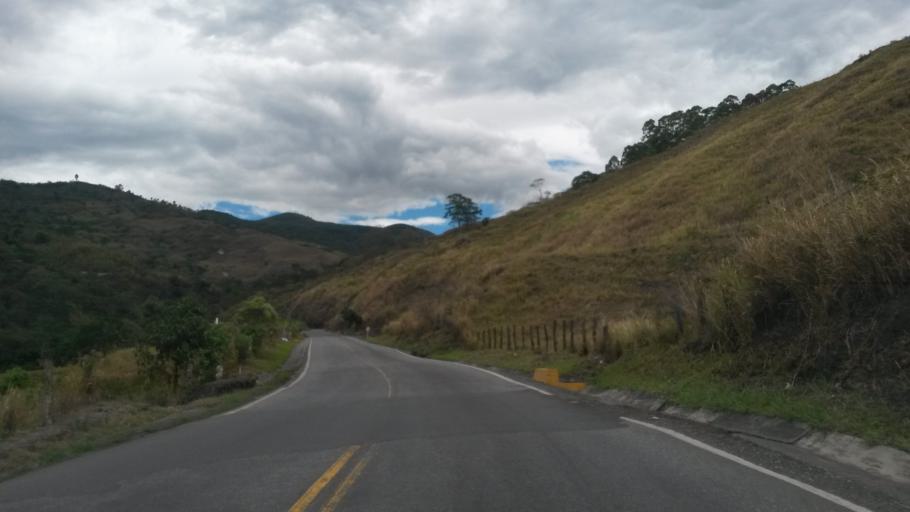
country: CO
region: Cauca
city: Rosas
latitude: 2.2802
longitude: -76.7077
